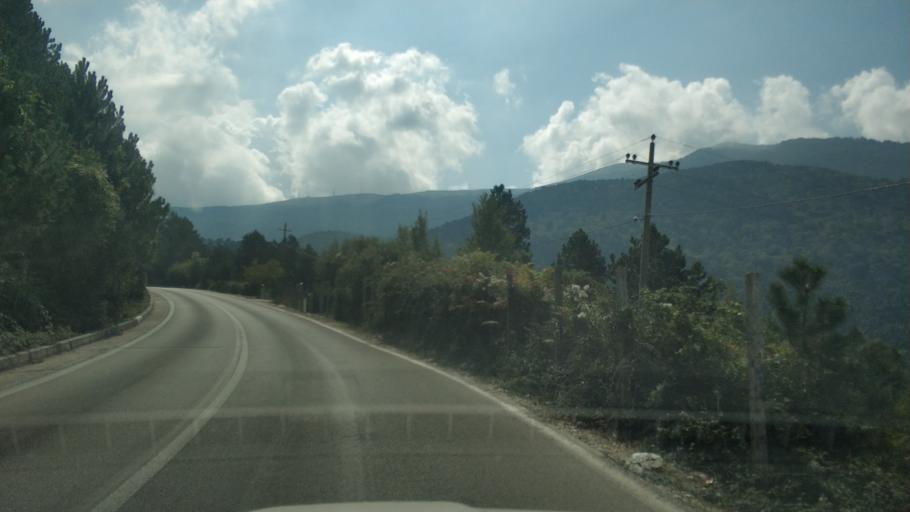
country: AL
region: Vlore
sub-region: Rrethi i Vlores
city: Brataj
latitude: 40.2287
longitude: 19.5778
